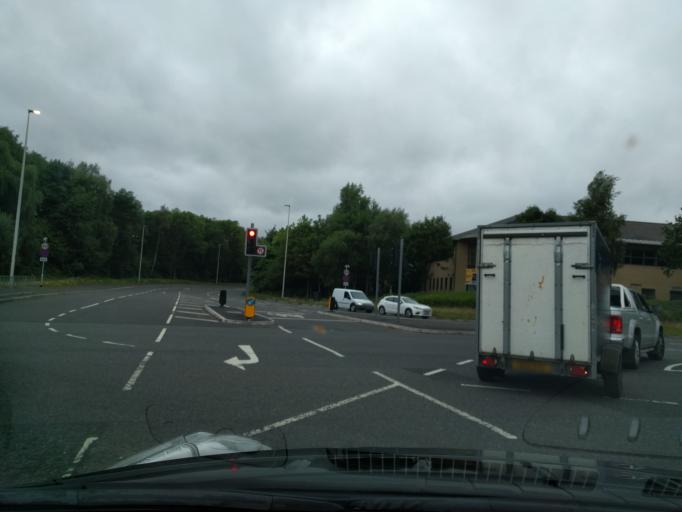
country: GB
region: England
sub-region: Warrington
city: Culcheth
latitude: 53.4285
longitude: -2.5132
